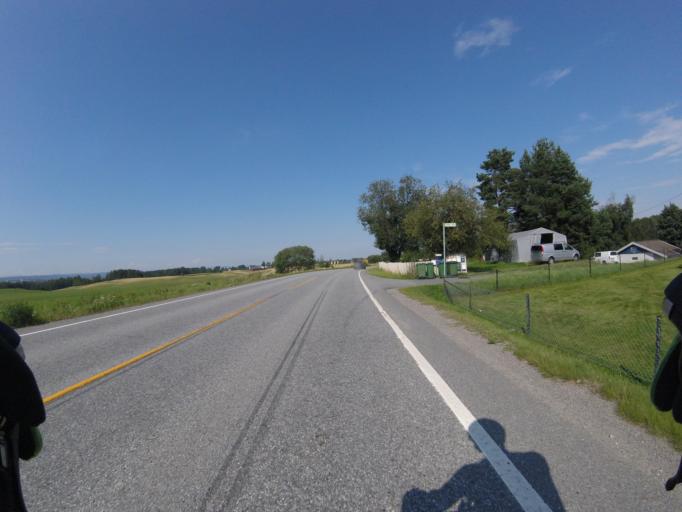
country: NO
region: Akershus
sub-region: Sorum
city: Frogner
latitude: 60.0416
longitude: 11.1137
